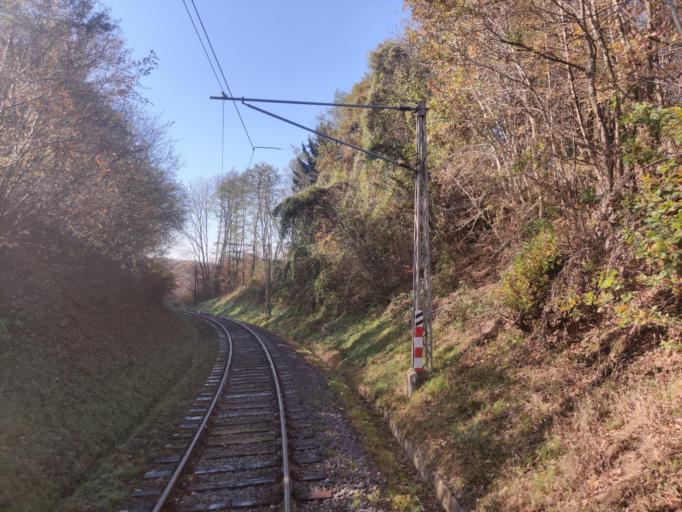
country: AT
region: Styria
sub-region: Politischer Bezirk Suedoststeiermark
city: Maierdorf
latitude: 46.8946
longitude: 15.8672
